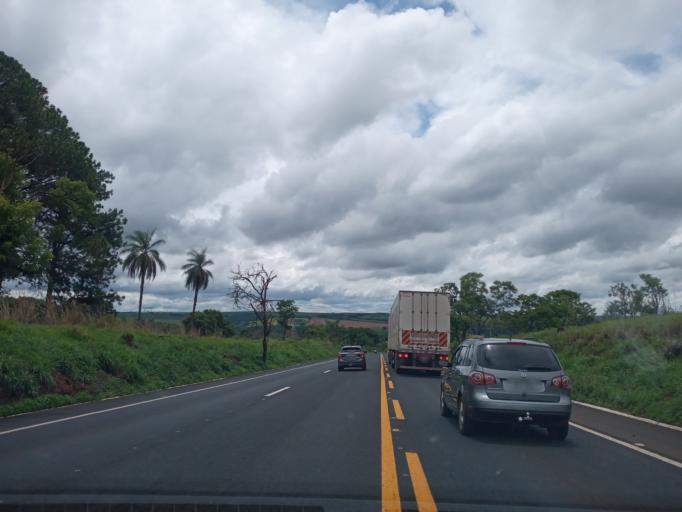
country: BR
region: Minas Gerais
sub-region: Uberaba
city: Uberaba
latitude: -19.2876
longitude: -47.6190
